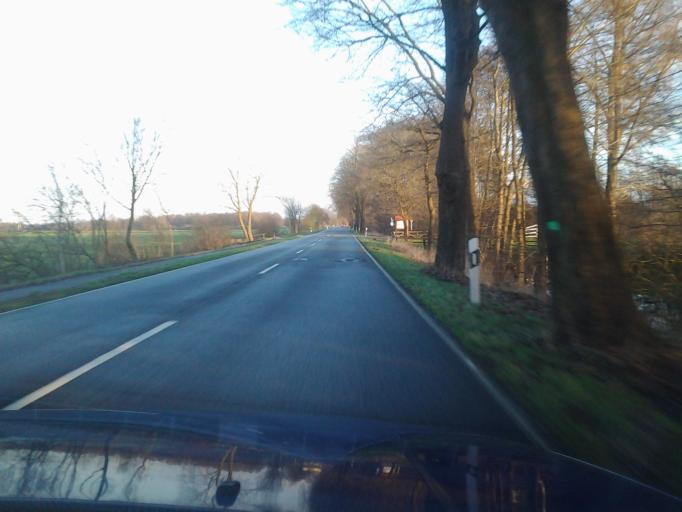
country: DE
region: Lower Saxony
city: Lilienthal
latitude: 53.1809
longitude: 8.8590
